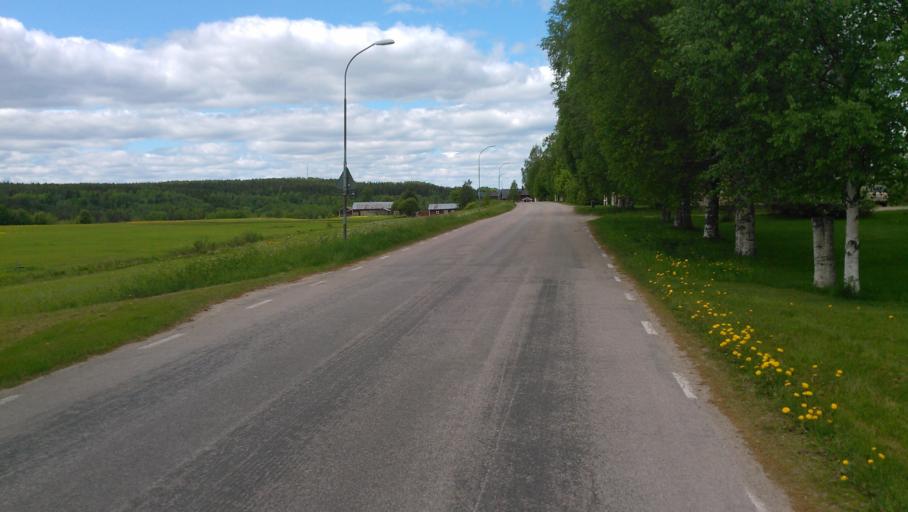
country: SE
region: Vaesterbotten
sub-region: Umea Kommun
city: Roback
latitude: 63.8644
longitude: 20.0826
